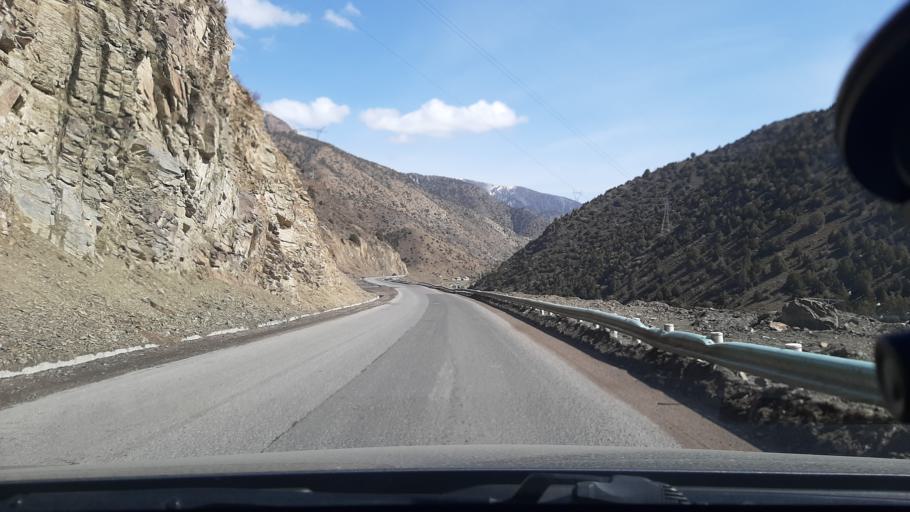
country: TJ
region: Viloyati Sughd
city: Ayni
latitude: 39.5658
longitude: 68.5896
